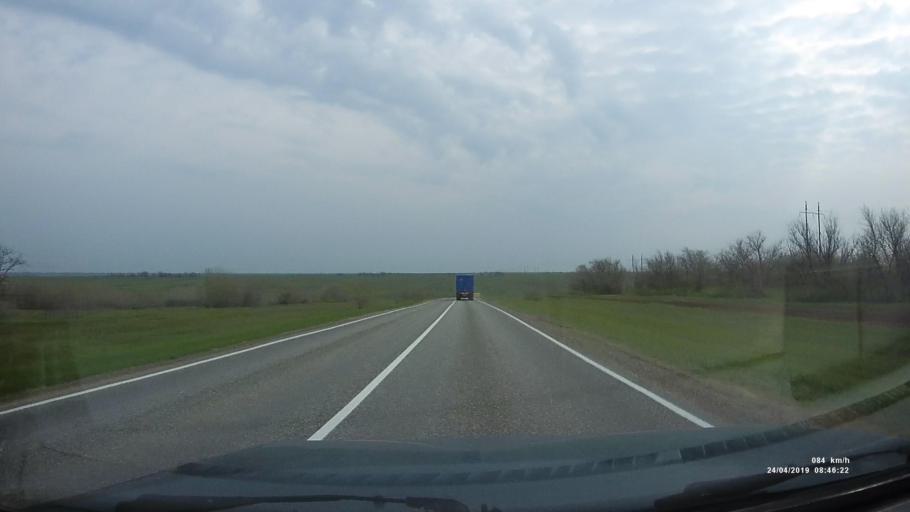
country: RU
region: Kalmykiya
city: Arshan'
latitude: 46.2383
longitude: 44.0774
